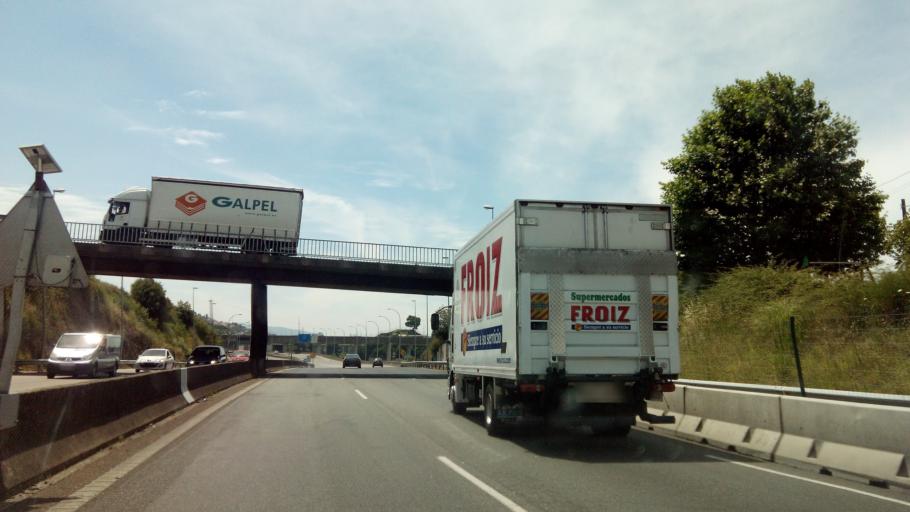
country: ES
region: Galicia
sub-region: Provincia de Pontevedra
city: Vigo
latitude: 42.2622
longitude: -8.6715
